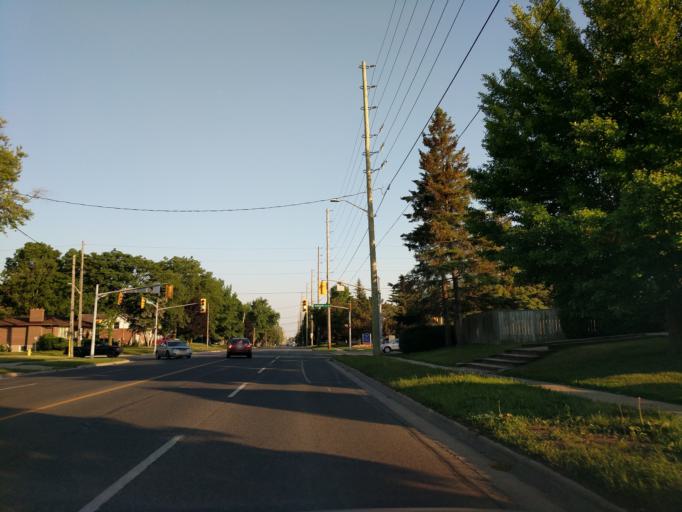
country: CA
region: Ontario
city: Oshawa
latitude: 43.8975
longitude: -78.8961
